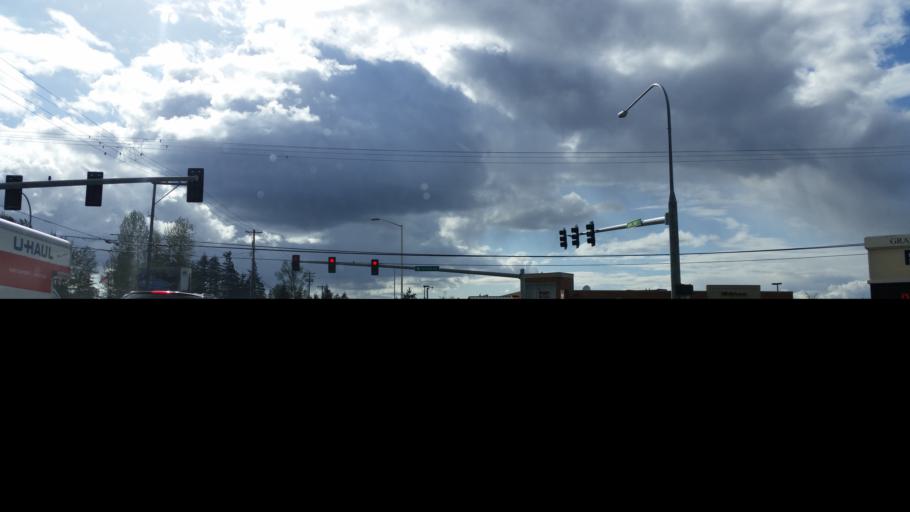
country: US
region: Washington
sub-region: Pierce County
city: Graham
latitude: 47.0531
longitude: -122.2941
